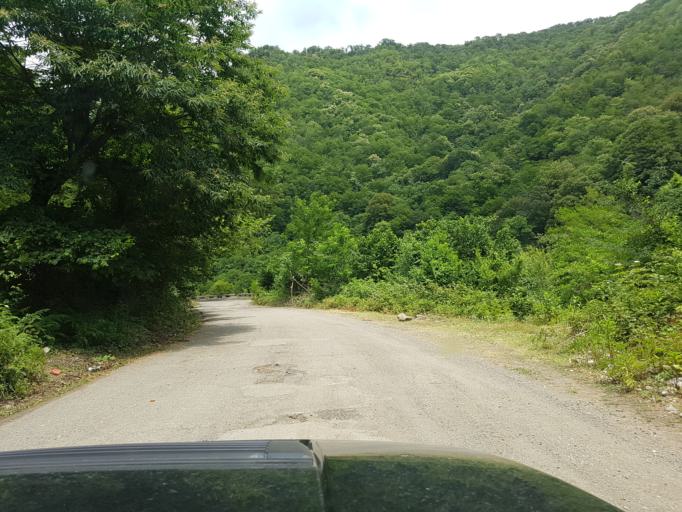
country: GE
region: Imereti
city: Tsqaltubo
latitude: 42.4179
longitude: 42.7135
